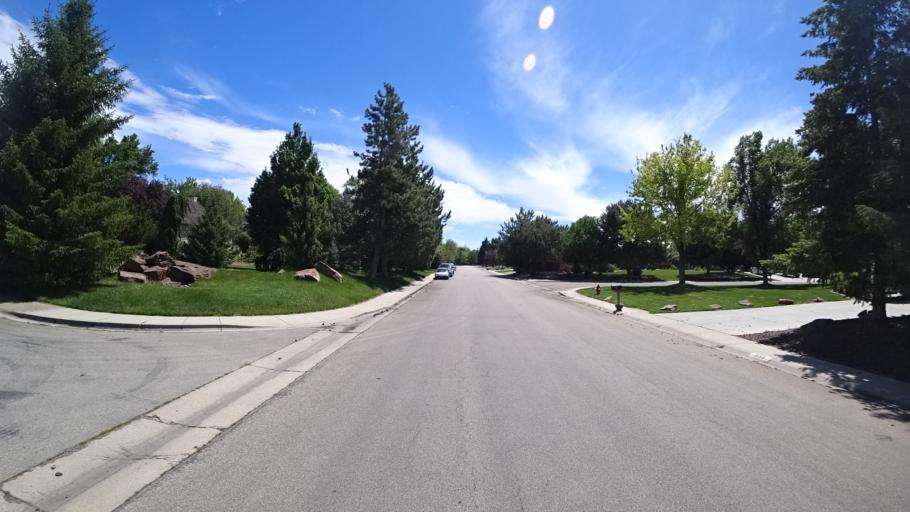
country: US
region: Idaho
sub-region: Ada County
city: Meridian
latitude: 43.5741
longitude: -116.3256
